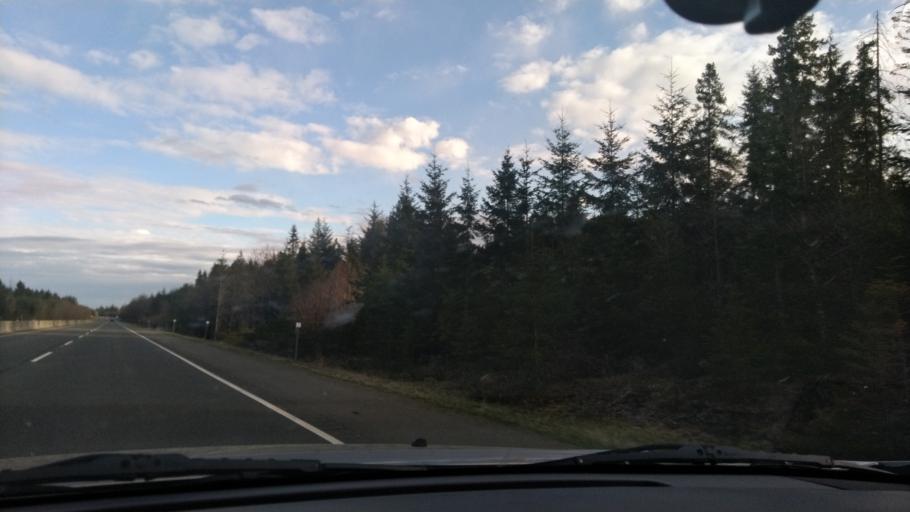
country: CA
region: British Columbia
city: Courtenay
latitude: 49.7569
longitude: -125.1296
